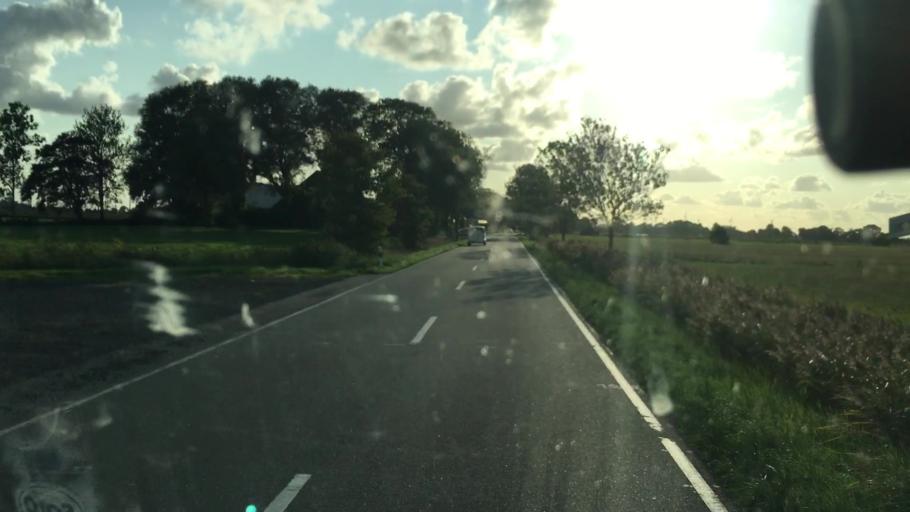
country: DE
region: Lower Saxony
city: Wittmund
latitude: 53.6426
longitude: 7.8057
